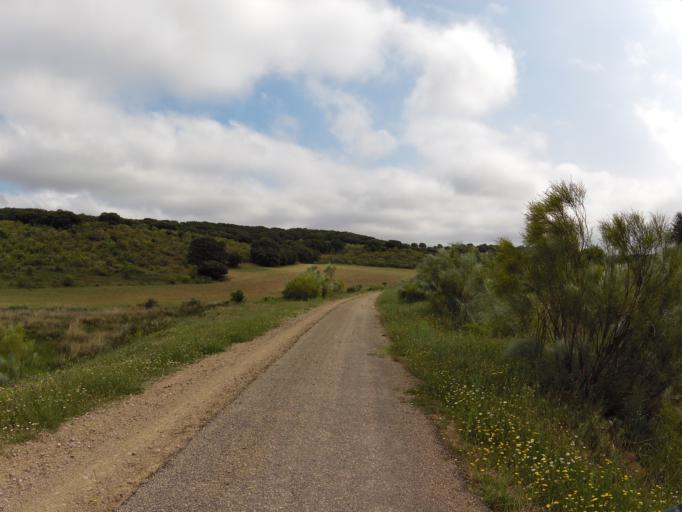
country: ES
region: Castille-La Mancha
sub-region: Provincia de Albacete
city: Alcaraz
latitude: 38.7169
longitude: -2.4915
